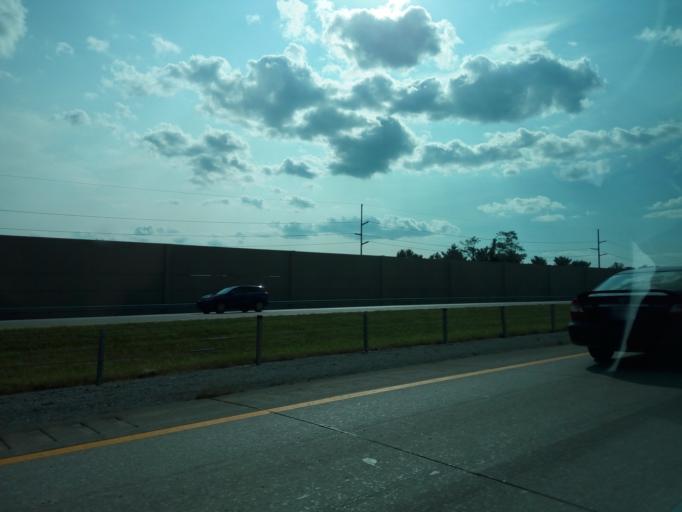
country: US
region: Kentucky
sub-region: Jefferson County
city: Worthington
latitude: 38.3048
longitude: -85.5615
